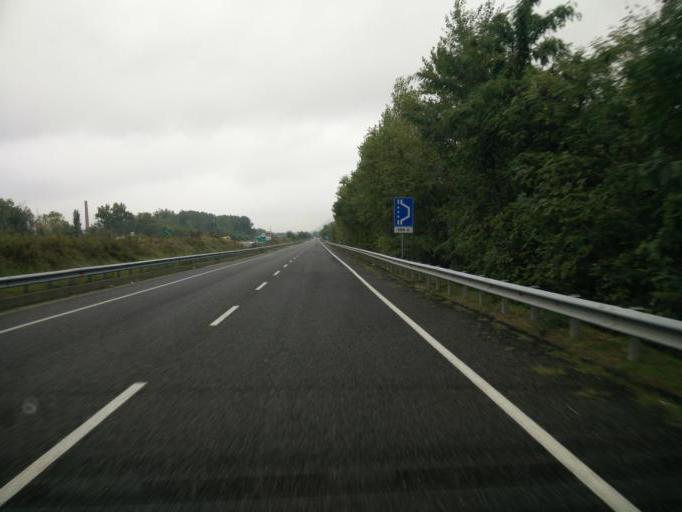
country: IT
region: Emilia-Romagna
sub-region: Provincia di Bologna
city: Borgonuovo
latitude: 44.4365
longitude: 11.2778
